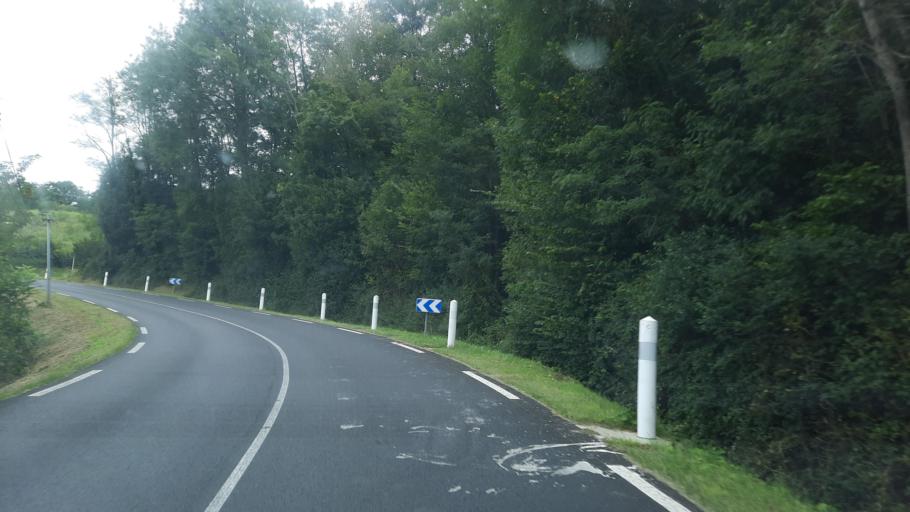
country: FR
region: Midi-Pyrenees
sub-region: Departement des Hautes-Pyrenees
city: Semeac
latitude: 43.2472
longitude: 0.1333
